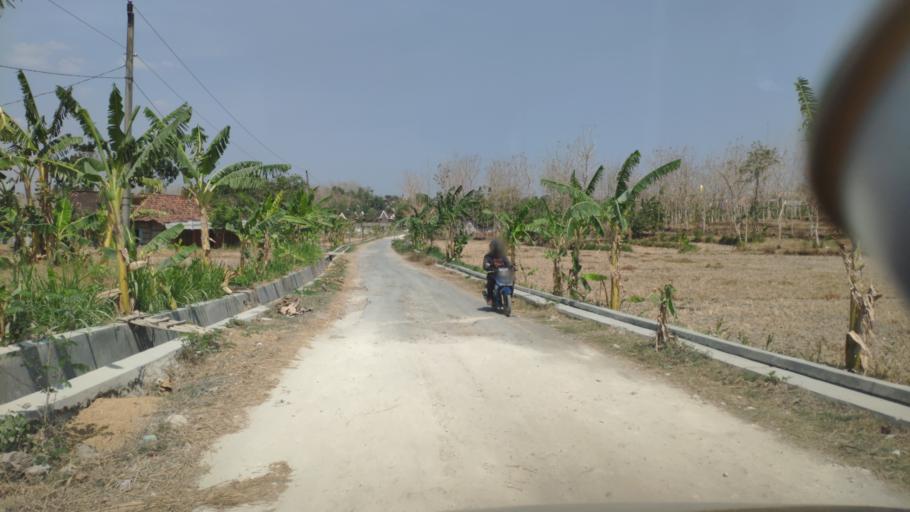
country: ID
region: Central Java
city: Pipes
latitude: -7.1034
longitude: 111.2506
